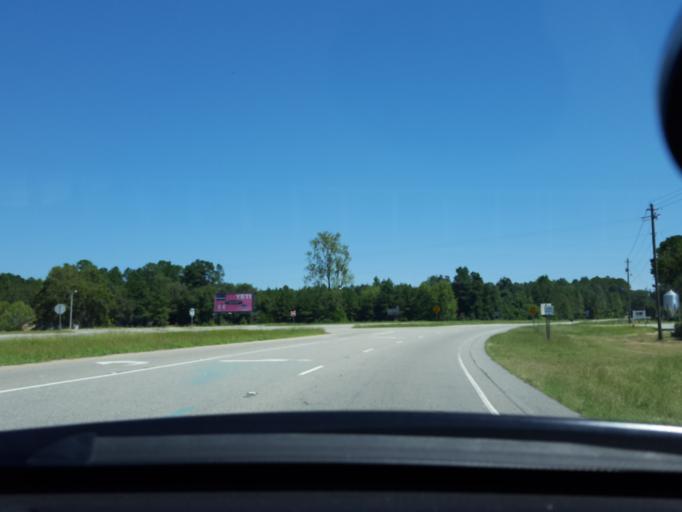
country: US
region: North Carolina
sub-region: Bladen County
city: Elizabethtown
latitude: 34.6440
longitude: -78.5934
